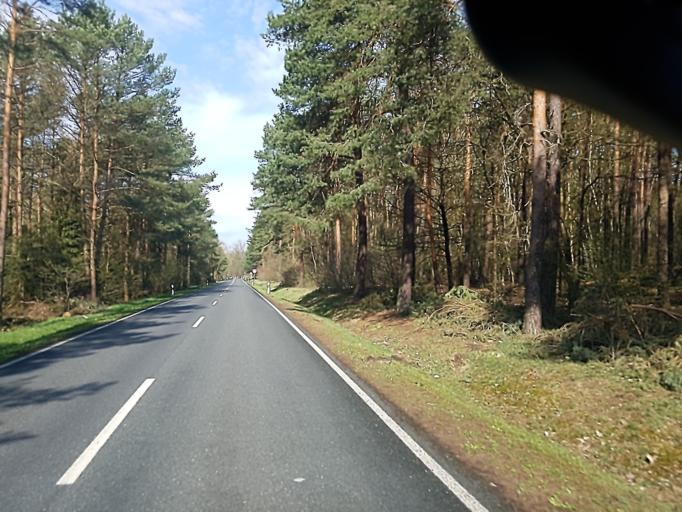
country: DE
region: Saxony
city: Kossa
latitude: 51.5772
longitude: 12.7372
